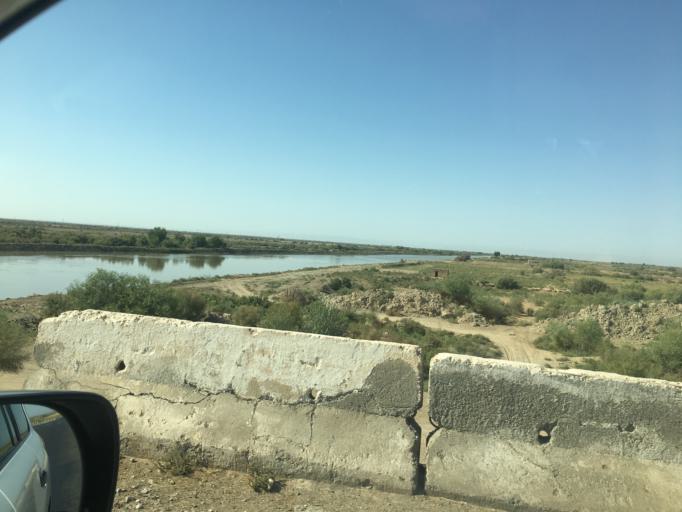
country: TM
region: Ahal
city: Tejen
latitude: 37.0764
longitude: 60.8539
